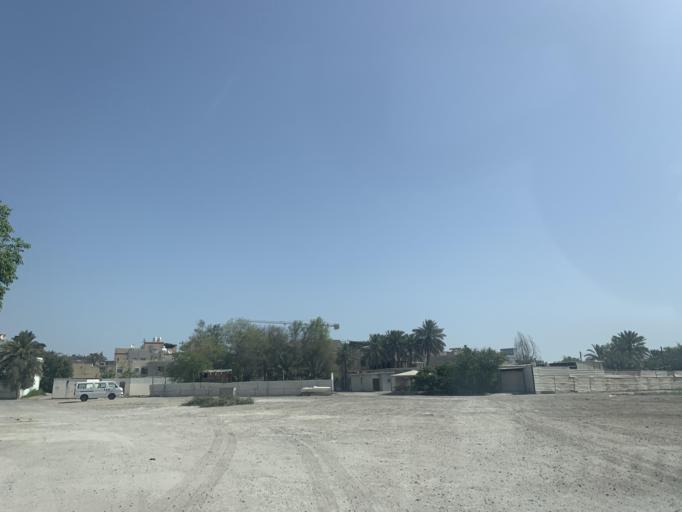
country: BH
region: Manama
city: Jidd Hafs
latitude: 26.2053
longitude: 50.5562
